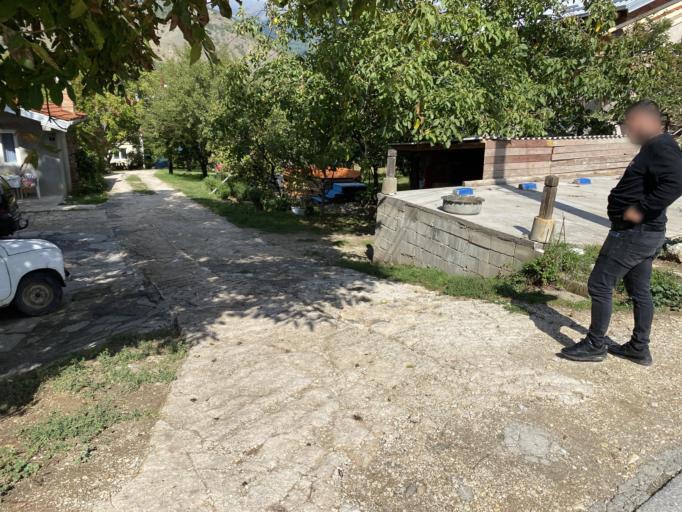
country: MK
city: Radishani
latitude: 42.1027
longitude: 21.4531
